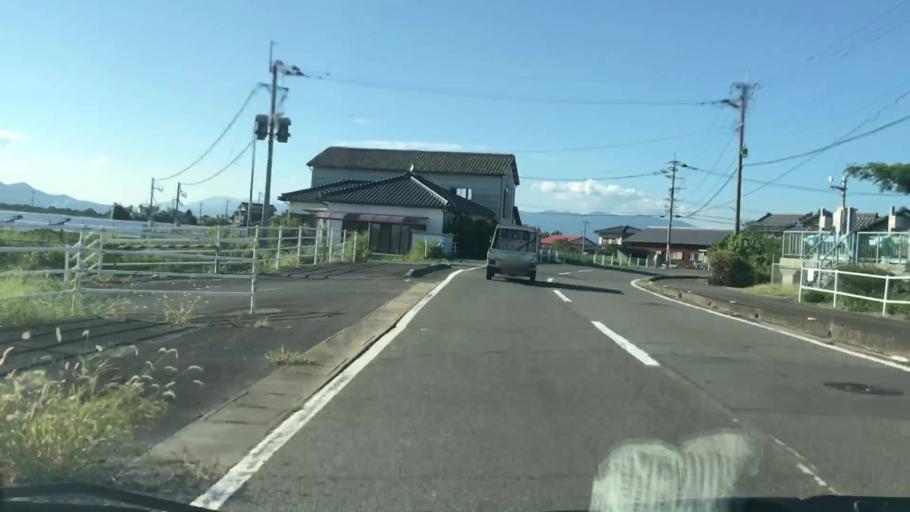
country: JP
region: Saga Prefecture
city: Saga-shi
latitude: 33.2011
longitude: 130.2658
